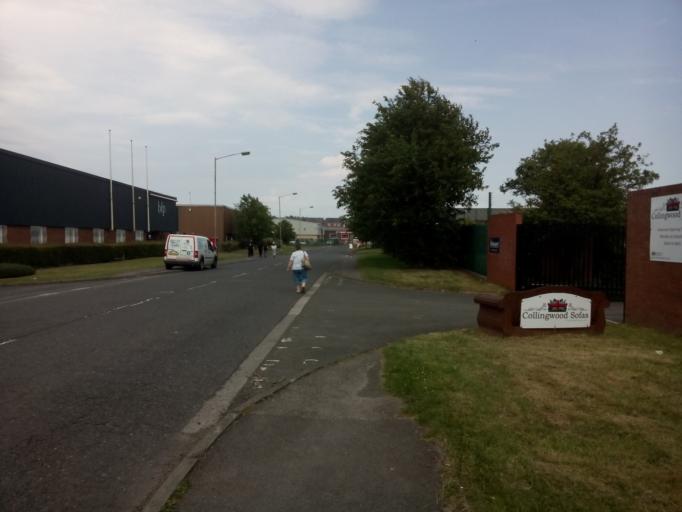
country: GB
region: England
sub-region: Northumberland
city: Backworth
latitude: 55.0206
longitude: -1.5423
